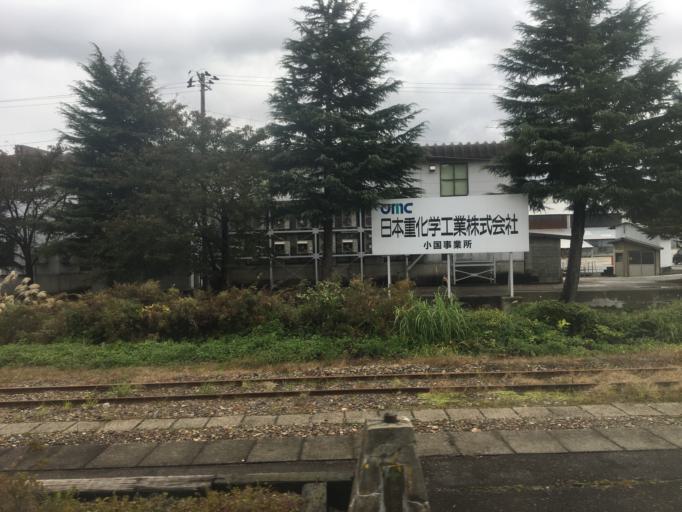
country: JP
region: Yamagata
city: Nagai
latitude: 38.0612
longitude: 139.7504
